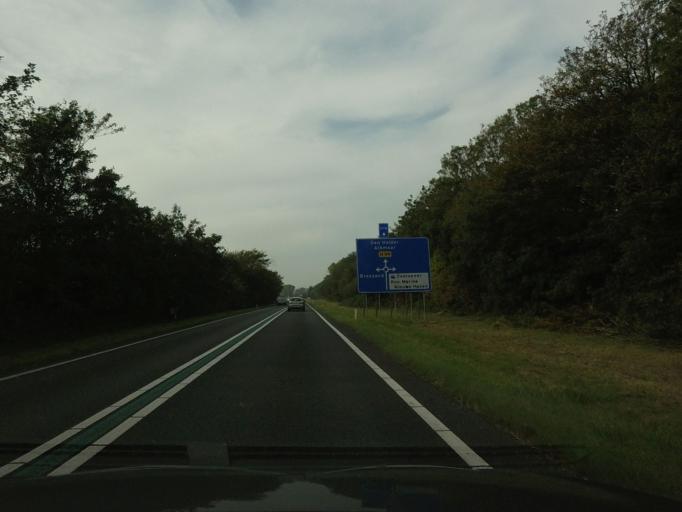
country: NL
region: North Holland
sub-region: Gemeente Den Helder
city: Den Helder
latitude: 52.9102
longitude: 4.8063
